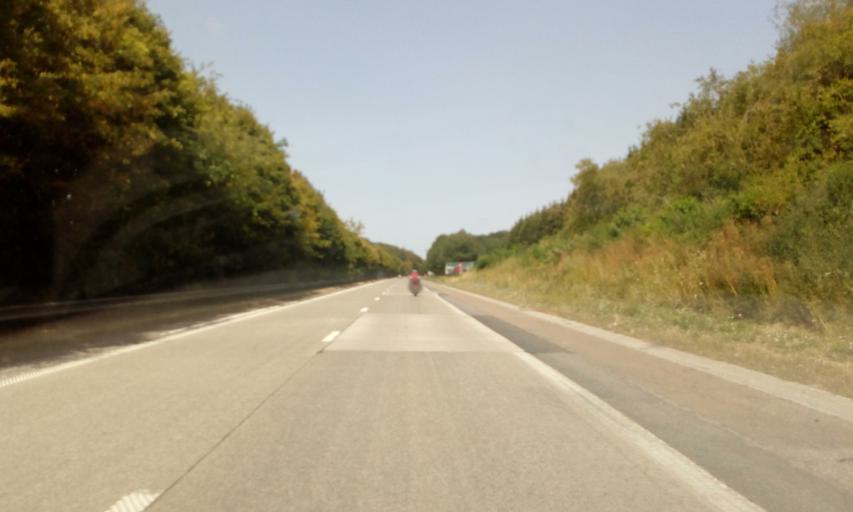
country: BE
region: Wallonia
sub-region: Province de Namur
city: Ciney
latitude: 50.2786
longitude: 5.0249
